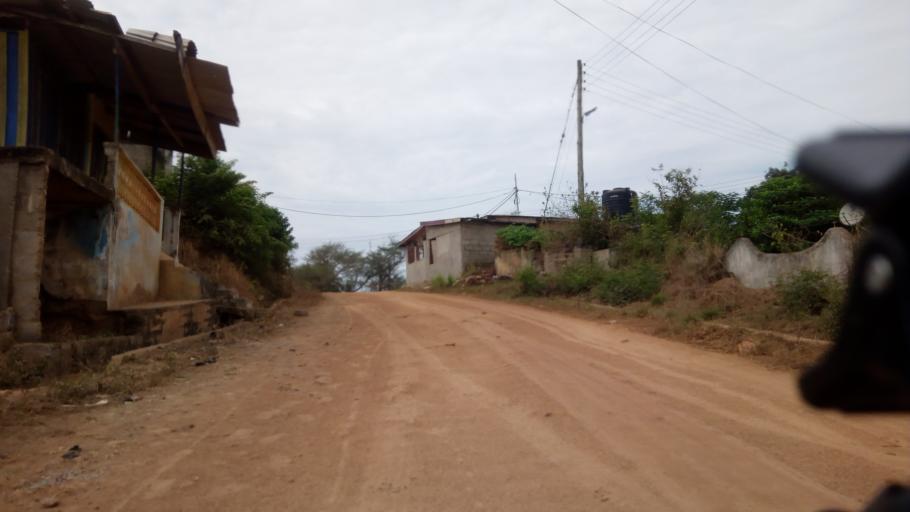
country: GH
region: Central
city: Cape Coast
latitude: 5.1050
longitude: -1.2709
